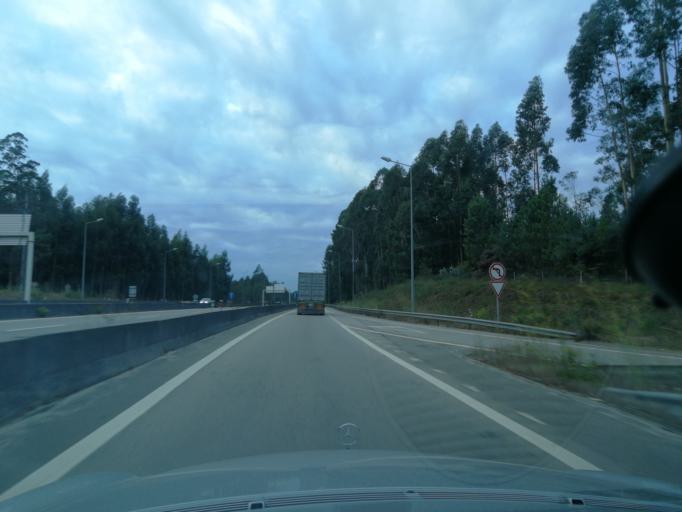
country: PT
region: Aveiro
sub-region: Albergaria-A-Velha
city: Albergaria-a-Velha
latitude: 40.6751
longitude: -8.4747
